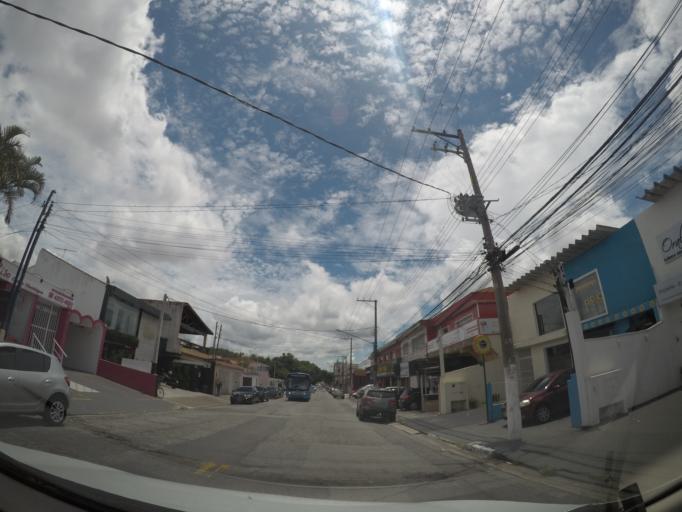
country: BR
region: Sao Paulo
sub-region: Guarulhos
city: Guarulhos
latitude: -23.4586
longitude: -46.5261
